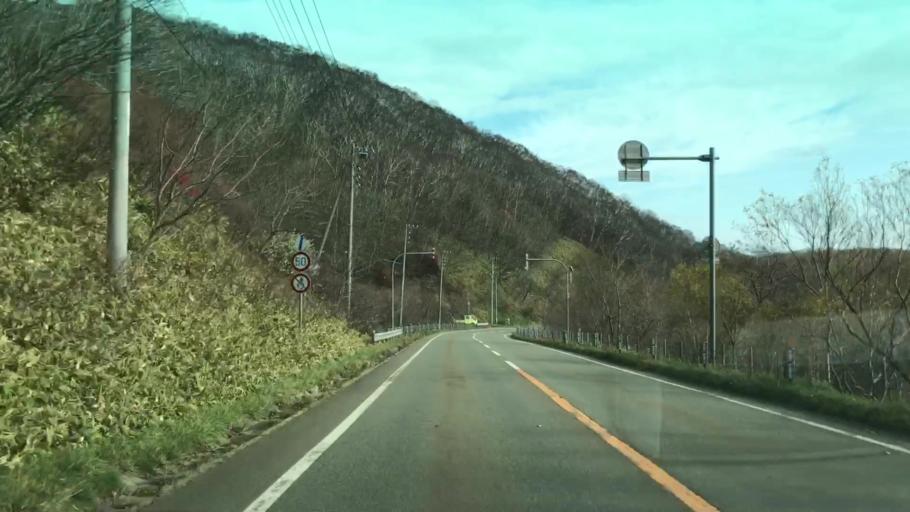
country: JP
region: Hokkaido
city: Obihiro
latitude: 42.0288
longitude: 143.2279
